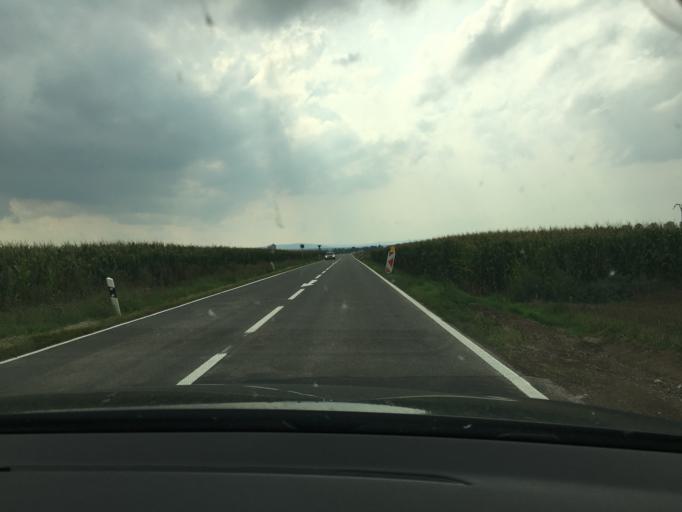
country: DE
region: North Rhine-Westphalia
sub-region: Regierungsbezirk Koln
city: Merzenich
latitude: 50.7903
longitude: 6.5682
